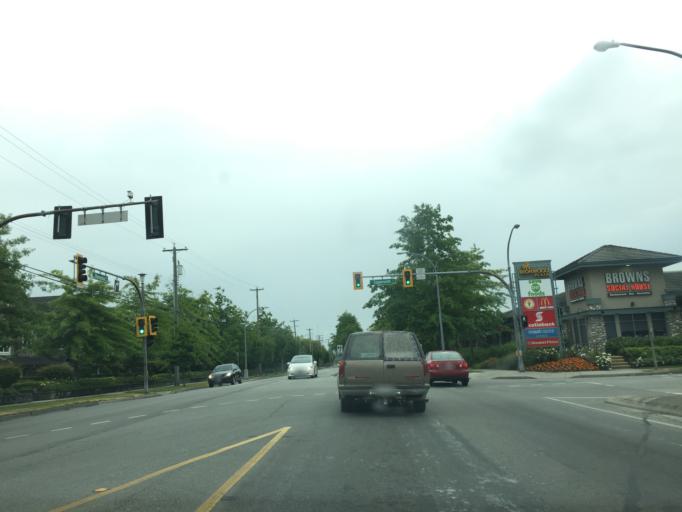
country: CA
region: British Columbia
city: Ladner
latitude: 49.1333
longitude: -123.0973
